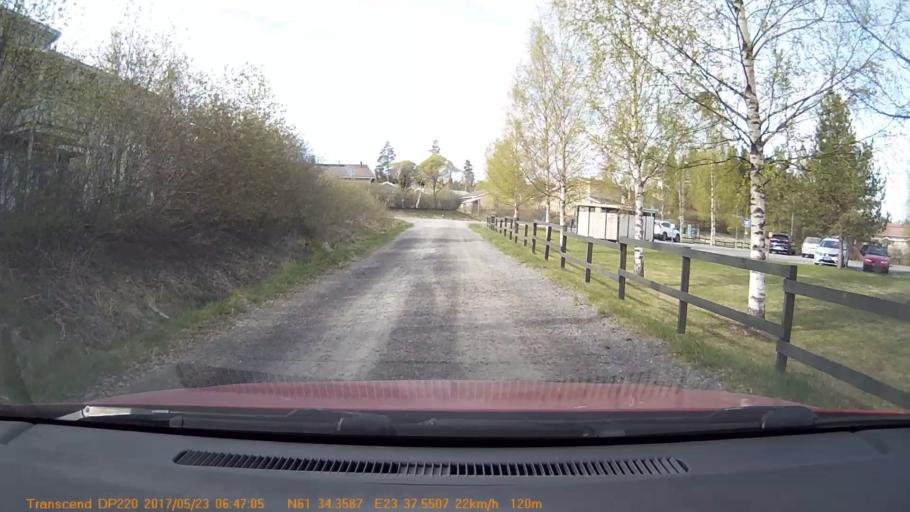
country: FI
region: Pirkanmaa
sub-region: Tampere
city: Yloejaervi
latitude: 61.5728
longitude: 23.6260
